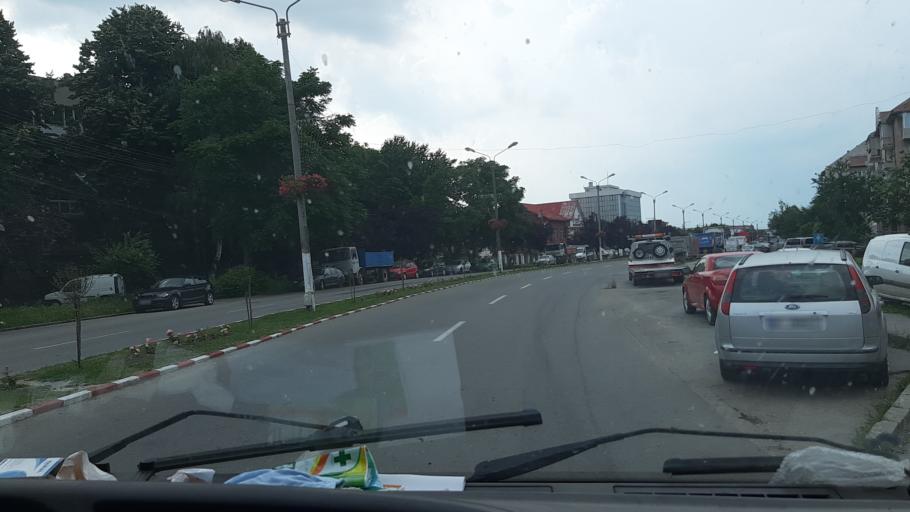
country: RO
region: Timis
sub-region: Municipiul Lugoj
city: Lugoj
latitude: 45.6977
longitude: 21.8969
